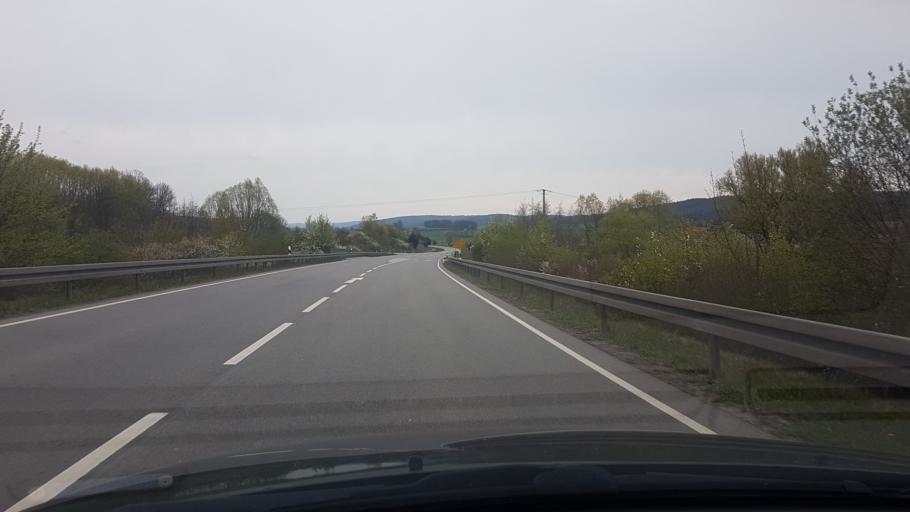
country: DE
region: Bavaria
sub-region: Upper Franconia
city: Reckendorf
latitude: 50.0318
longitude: 10.8255
